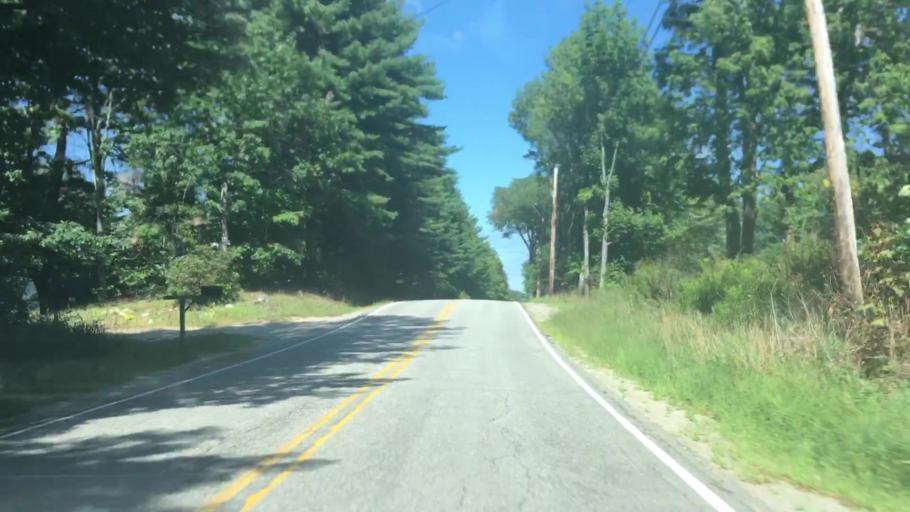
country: US
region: Maine
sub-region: Kennebec County
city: Monmouth
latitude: 44.1788
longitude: -69.9401
